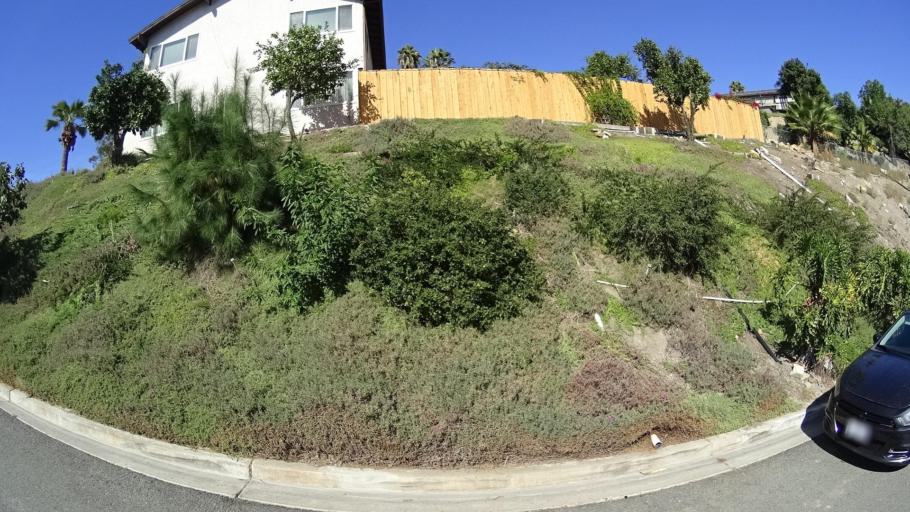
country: US
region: California
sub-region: San Diego County
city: Casa de Oro-Mount Helix
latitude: 32.7558
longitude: -116.9830
